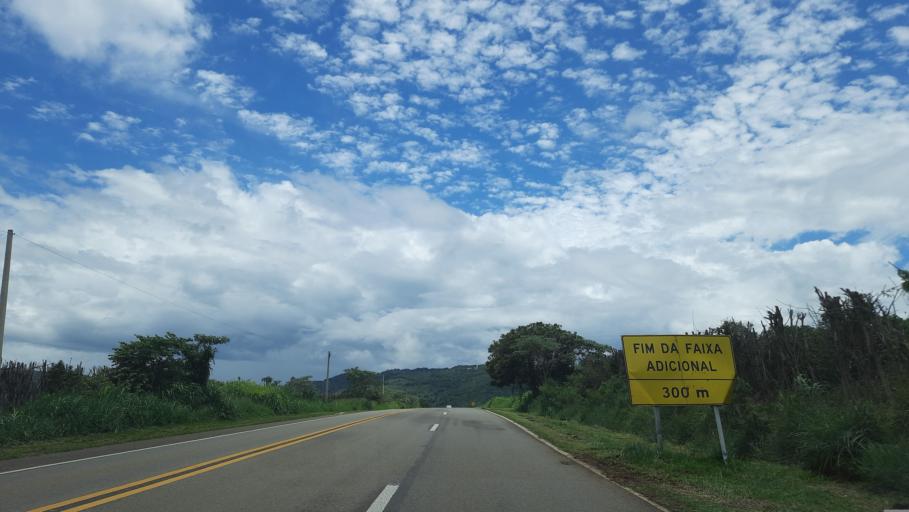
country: BR
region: Sao Paulo
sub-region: Vargem Grande Do Sul
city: Vargem Grande do Sul
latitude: -21.8111
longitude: -46.7889
